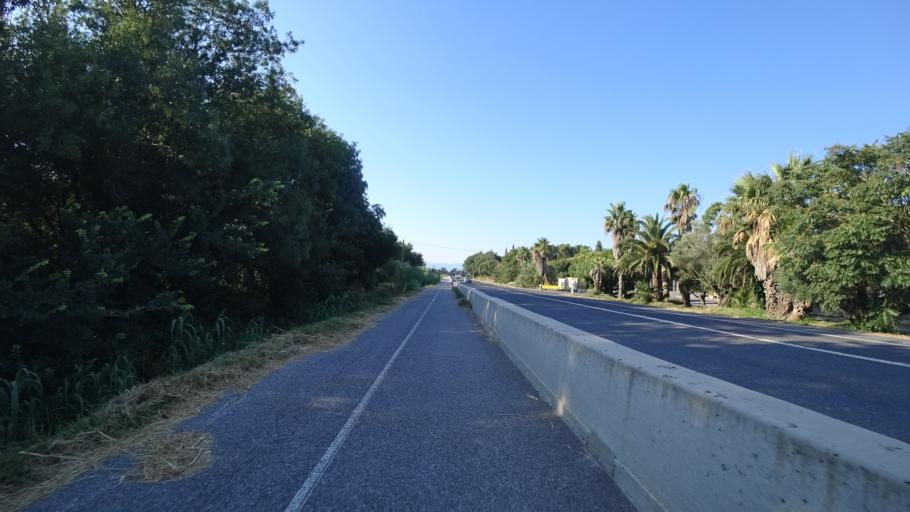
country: FR
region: Languedoc-Roussillon
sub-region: Departement des Pyrenees-Orientales
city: Canet-en-Roussillon
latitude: 42.6982
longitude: 3.0002
